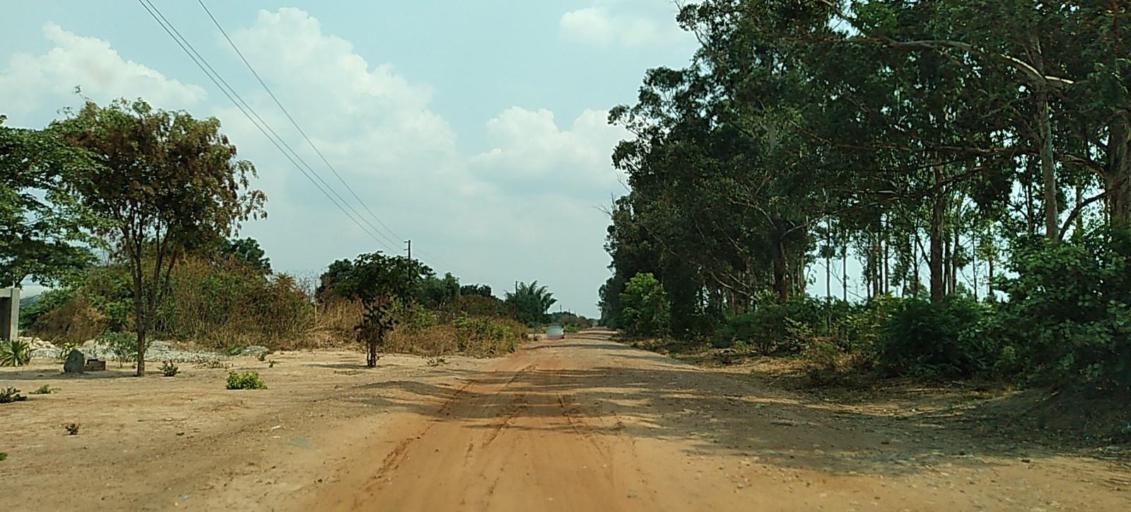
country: ZM
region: Copperbelt
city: Kalulushi
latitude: -12.8272
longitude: 28.0771
